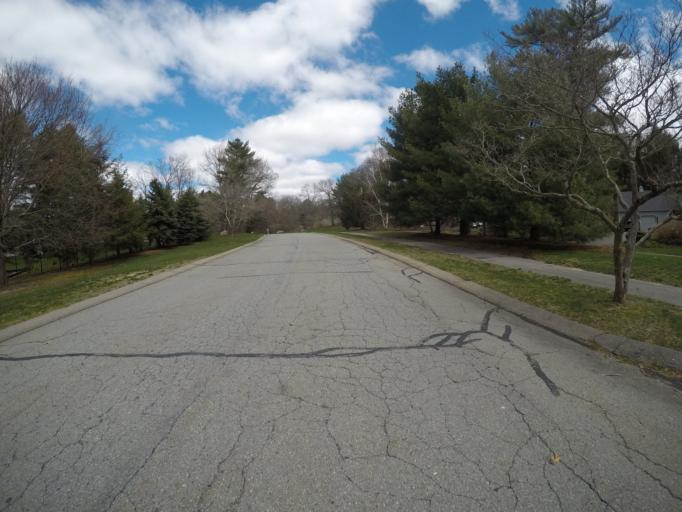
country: US
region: Massachusetts
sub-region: Norfolk County
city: Stoughton
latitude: 42.0761
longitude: -71.0964
